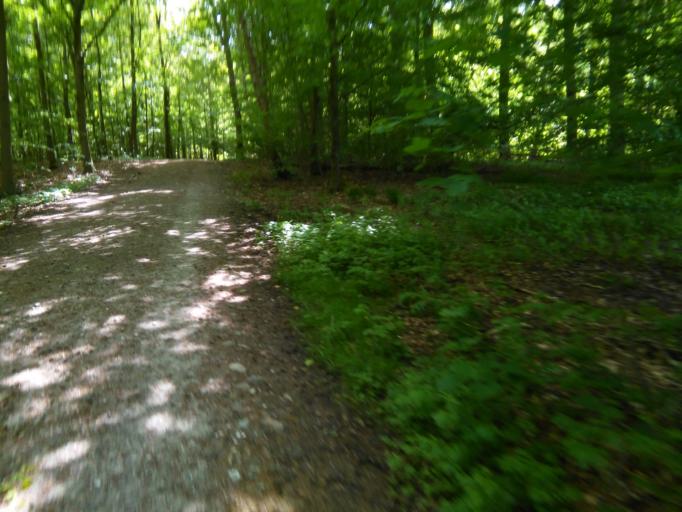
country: DK
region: Central Jutland
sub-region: Arhus Kommune
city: Beder
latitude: 56.0662
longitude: 10.2486
